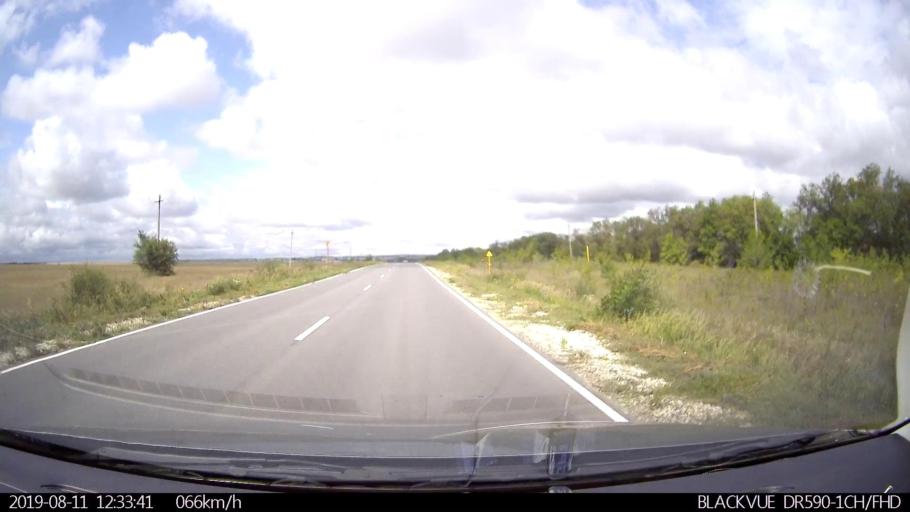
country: RU
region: Ulyanovsk
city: Ignatovka
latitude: 53.8112
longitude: 47.8529
